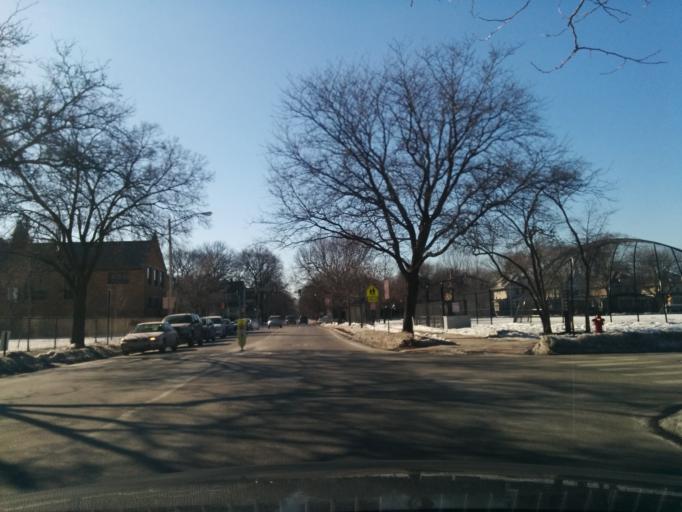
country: US
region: Illinois
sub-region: Cook County
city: Oak Park
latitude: 41.8763
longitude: -87.7829
